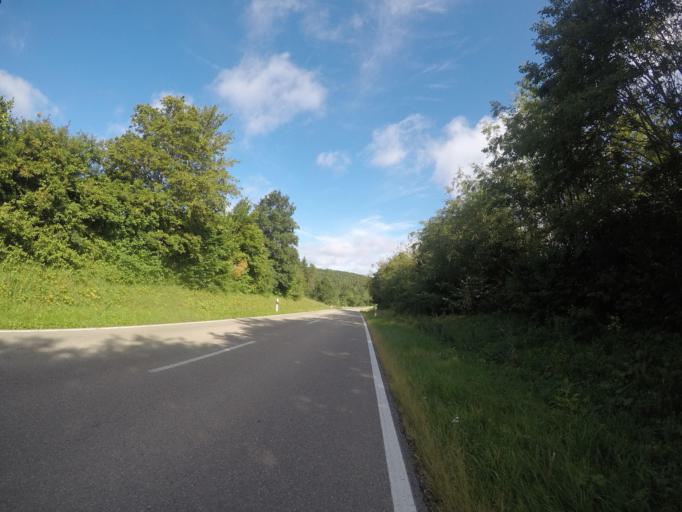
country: DE
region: Baden-Wuerttemberg
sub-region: Tuebingen Region
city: Laichingen
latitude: 48.4096
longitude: 9.6509
